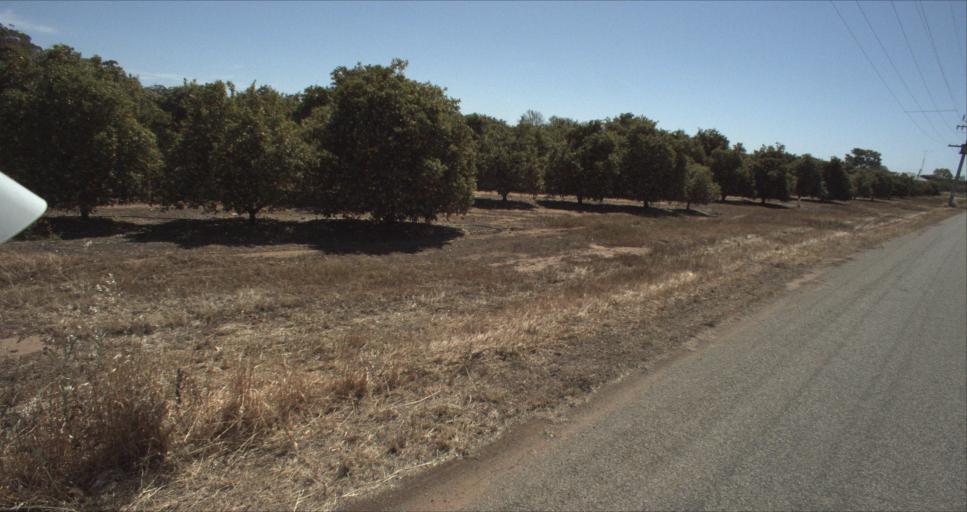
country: AU
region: New South Wales
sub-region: Leeton
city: Leeton
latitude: -34.5441
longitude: 146.3535
